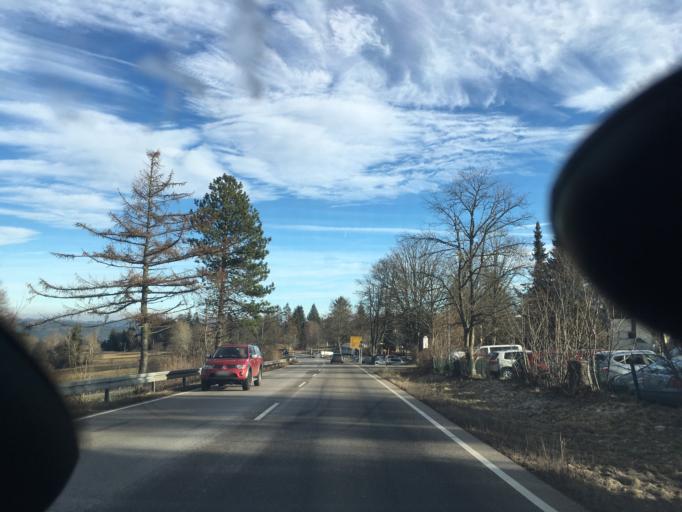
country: DE
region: Baden-Wuerttemberg
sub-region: Freiburg Region
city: Hochenschwand
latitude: 47.7375
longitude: 8.1654
